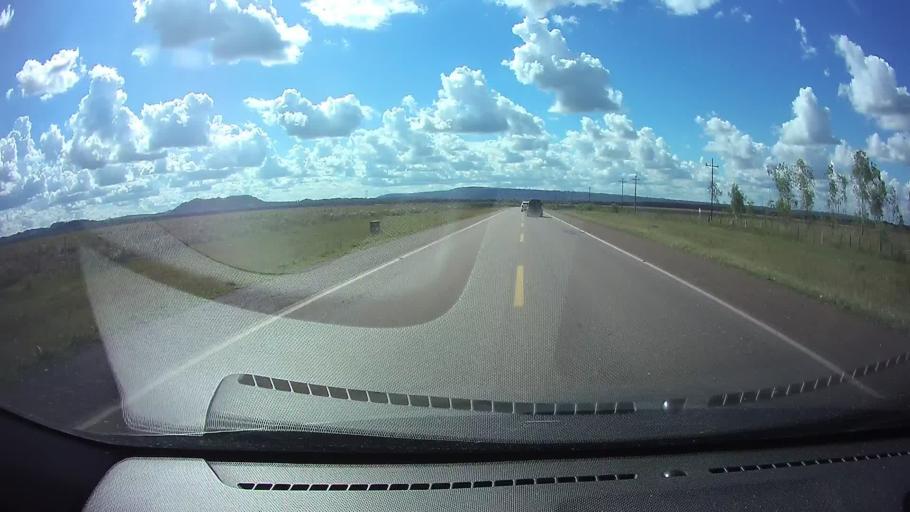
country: PY
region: Paraguari
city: Sapucai
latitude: -25.7385
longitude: -56.8129
